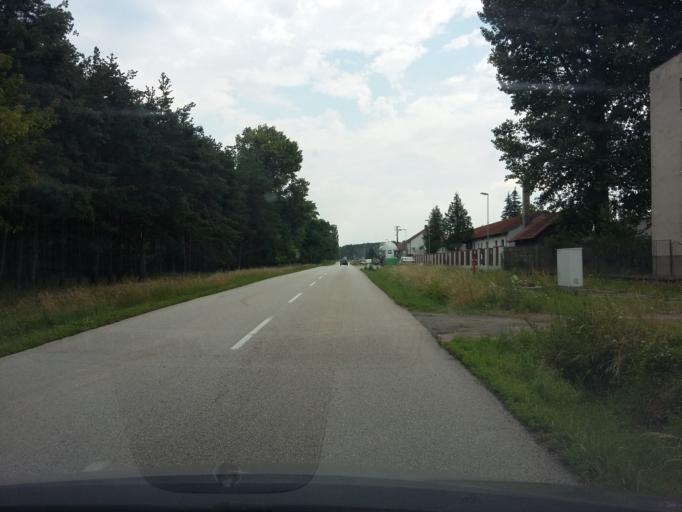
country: SK
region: Bratislavsky
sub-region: Okres Malacky
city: Malacky
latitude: 48.4434
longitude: 17.0498
